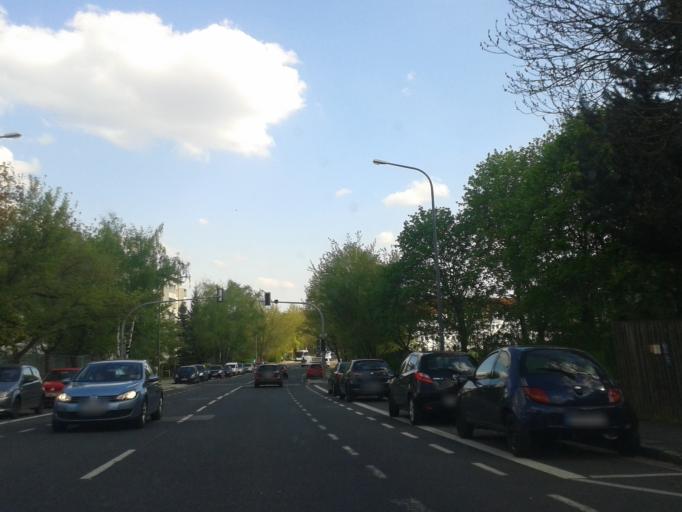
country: DE
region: Saxony
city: Albertstadt
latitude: 51.1151
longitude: 13.7717
